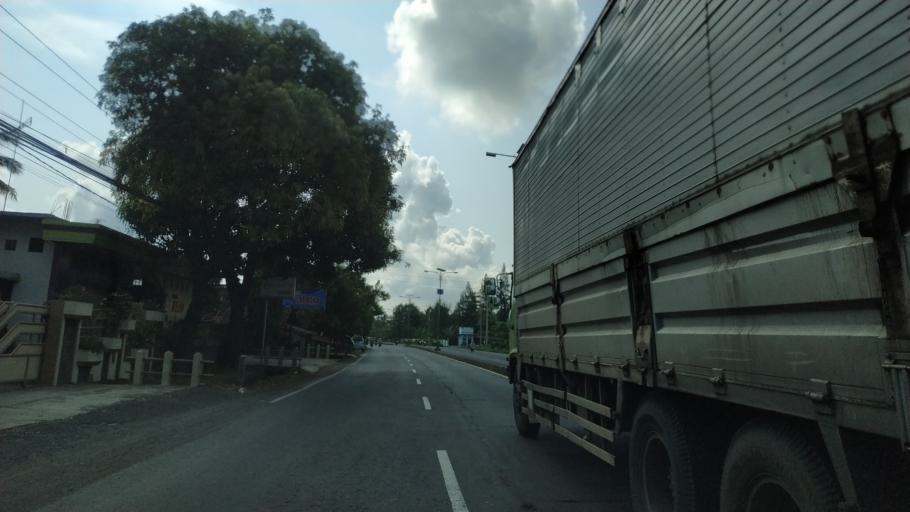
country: ID
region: Central Java
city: Comal
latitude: -6.8981
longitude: 109.5378
